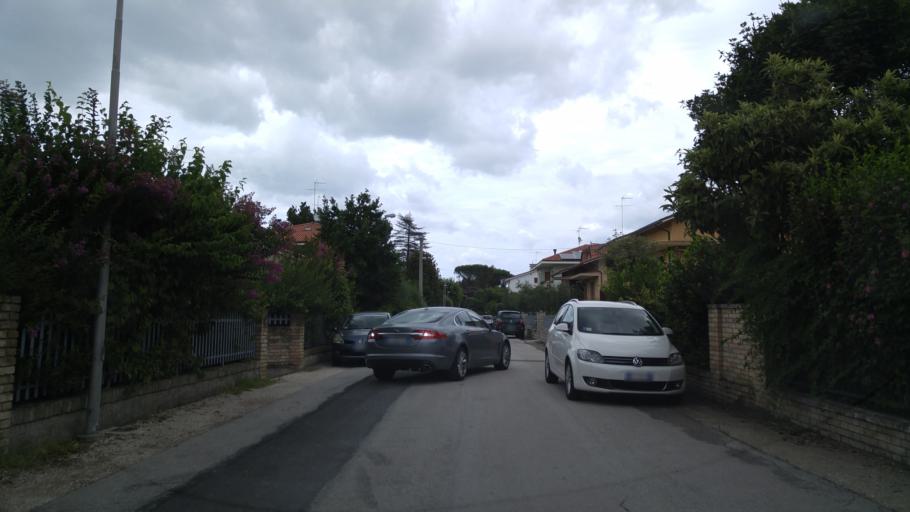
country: IT
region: The Marches
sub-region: Provincia di Pesaro e Urbino
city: Fano
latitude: 43.8469
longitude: 13.0025
